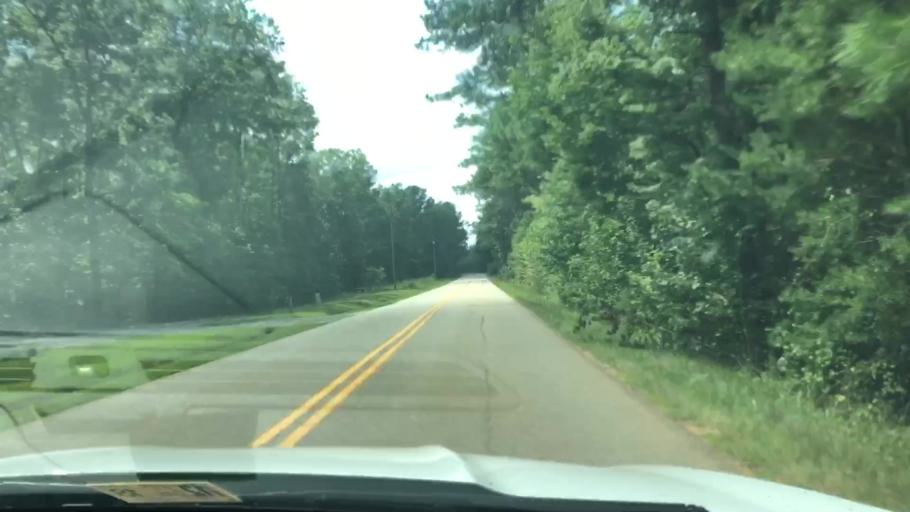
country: US
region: Virginia
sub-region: King William County
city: West Point
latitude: 37.6111
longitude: -76.7121
